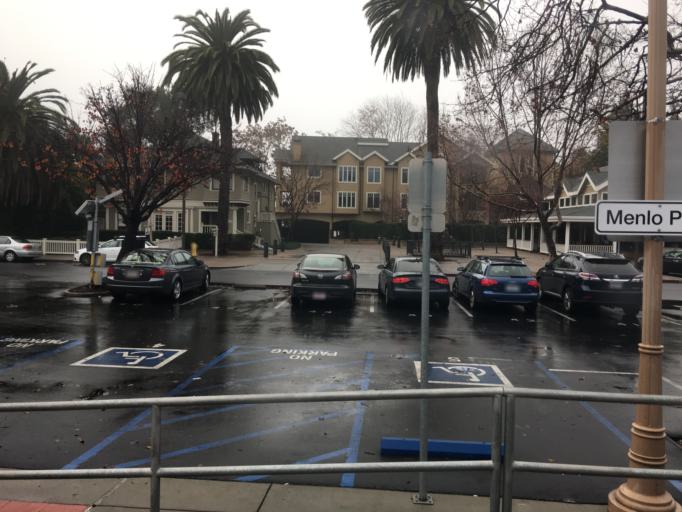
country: US
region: California
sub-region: San Mateo County
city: Menlo Park
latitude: 37.4551
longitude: -122.1828
